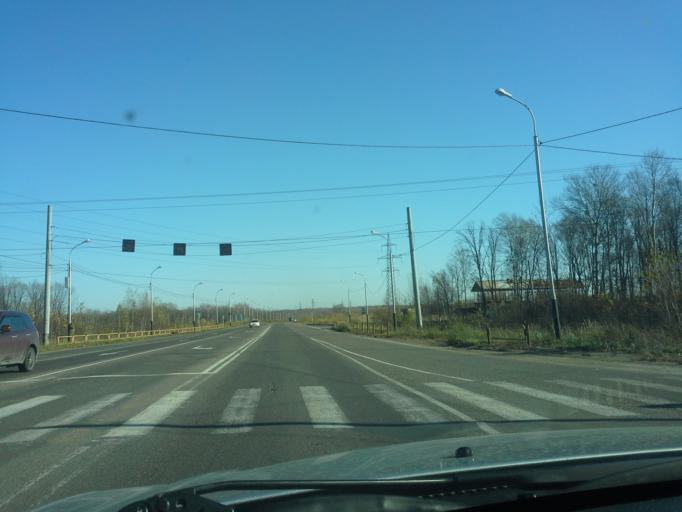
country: RU
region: Khabarovsk Krai
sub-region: Khabarovskiy Rayon
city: Khabarovsk
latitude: 48.5472
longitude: 135.0958
